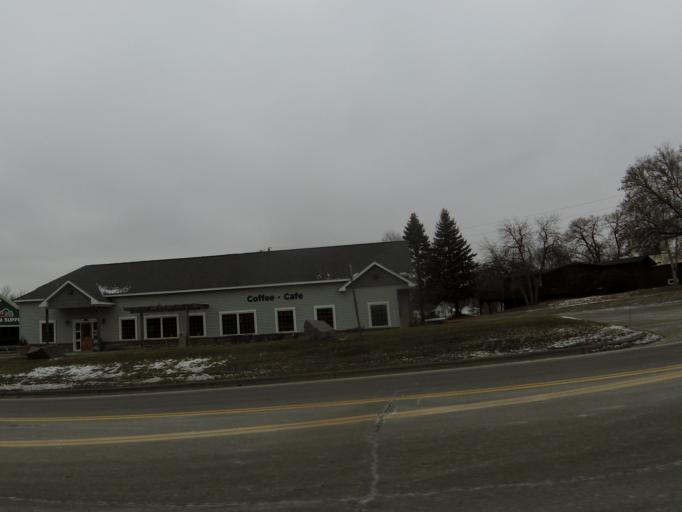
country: US
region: Minnesota
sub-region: Hennepin County
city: Maple Plain
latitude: 45.0070
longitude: -93.6540
